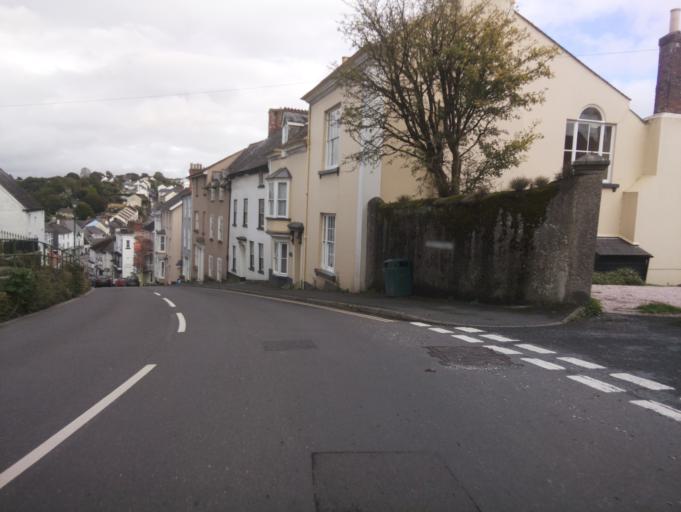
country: GB
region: England
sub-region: Devon
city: Modbury
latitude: 50.3493
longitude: -3.8895
